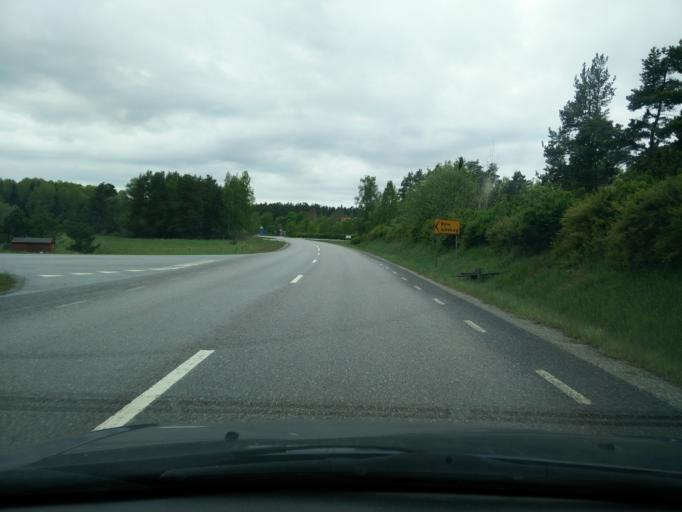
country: SE
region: Stockholm
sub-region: Norrtalje Kommun
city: Bjorko
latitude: 59.8207
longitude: 18.9066
